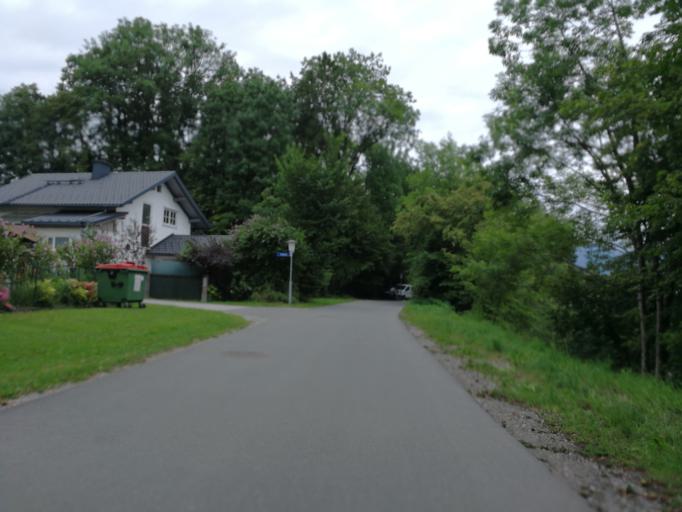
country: DE
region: Bavaria
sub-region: Upper Bavaria
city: Ainring
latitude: 47.7936
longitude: 12.9560
